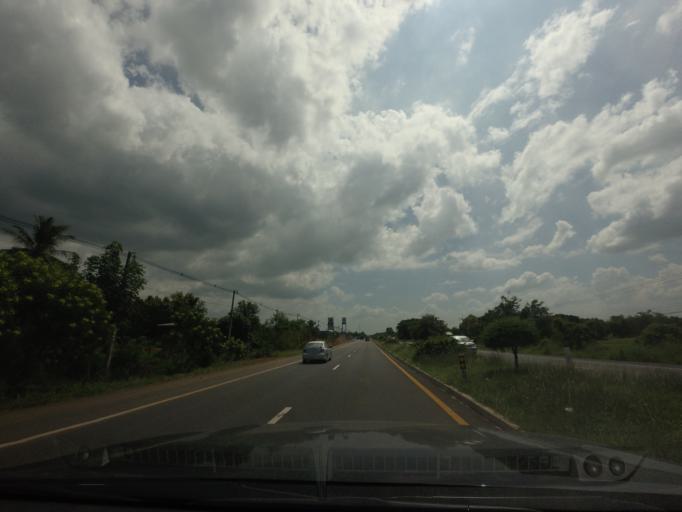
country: TH
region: Phetchabun
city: Nong Phai
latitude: 16.2070
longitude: 101.0890
